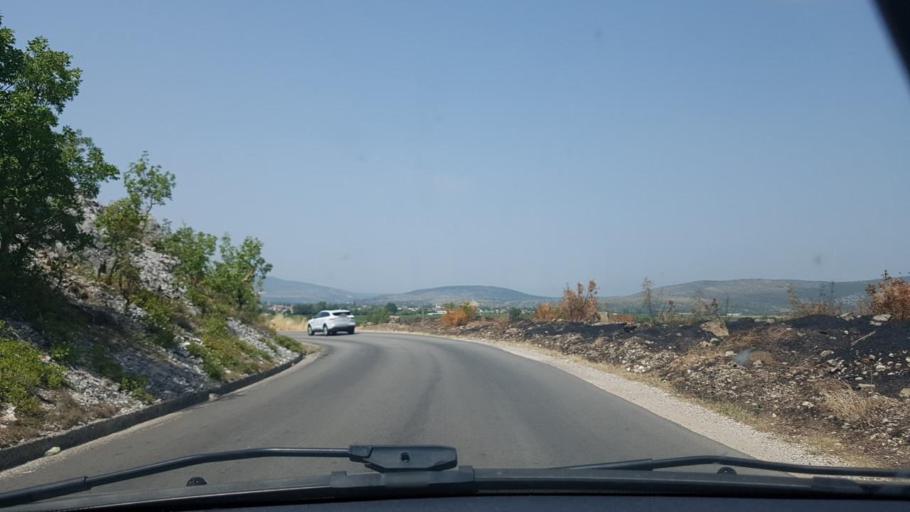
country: HR
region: Dubrovacko-Neretvanska
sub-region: Grad Dubrovnik
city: Metkovic
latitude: 43.0420
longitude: 17.7097
